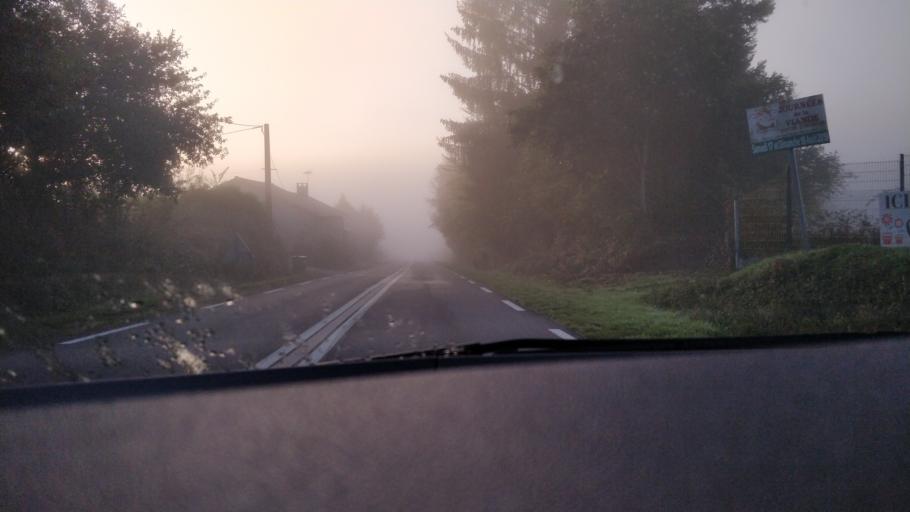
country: FR
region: Limousin
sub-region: Departement de la Haute-Vienne
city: Saint-Leonard-de-Noblat
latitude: 45.8460
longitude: 1.4580
